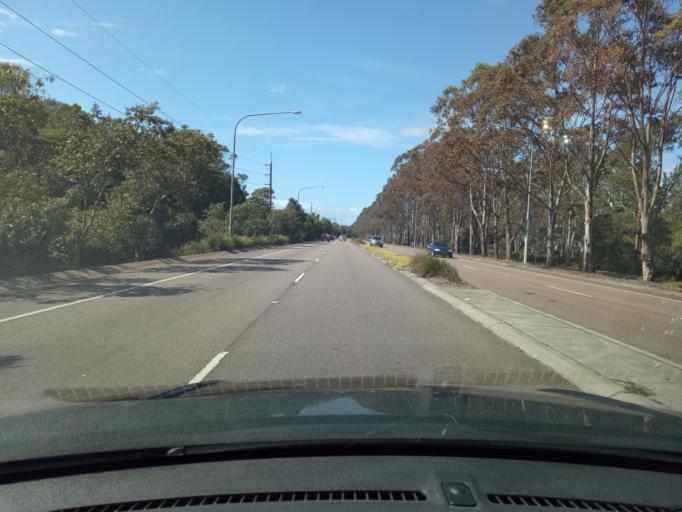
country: AU
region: New South Wales
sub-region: Wyong Shire
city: Chittaway Bay
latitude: -33.3161
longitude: 151.4243
